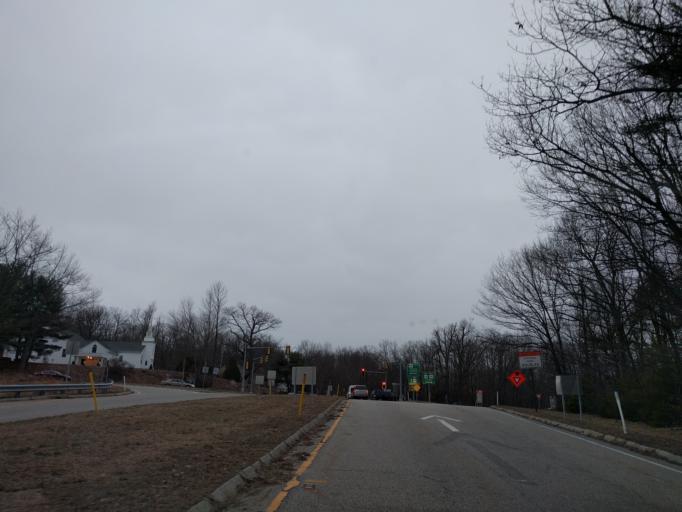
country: US
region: Massachusetts
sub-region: Worcester County
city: Westminster
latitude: 42.5418
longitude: -71.8967
